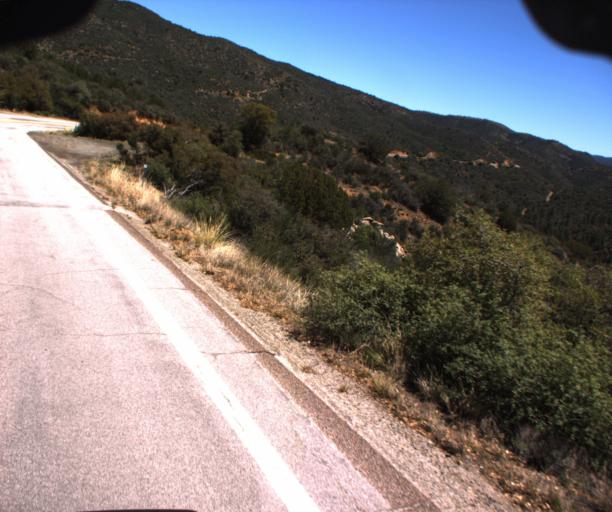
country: US
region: Arizona
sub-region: Yavapai County
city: Prescott
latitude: 34.4493
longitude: -112.5393
